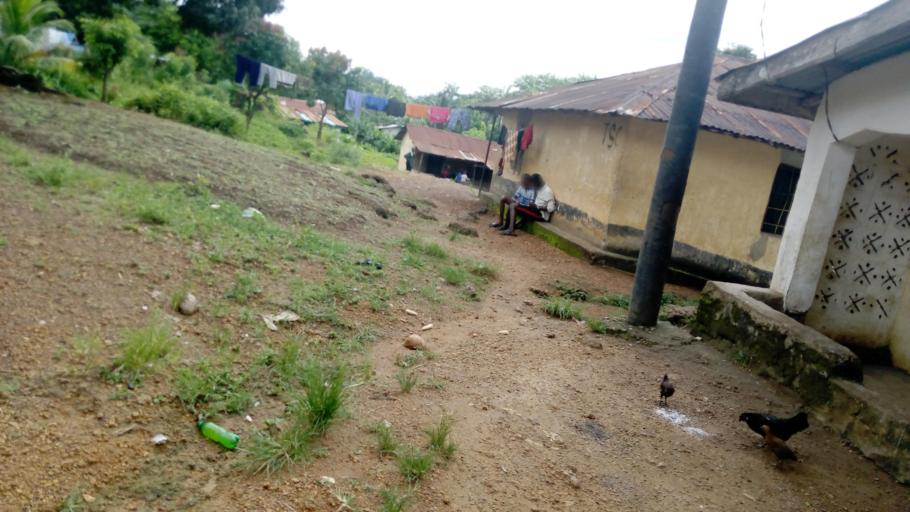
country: SL
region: Northern Province
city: Makeni
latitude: 8.8855
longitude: -12.0315
